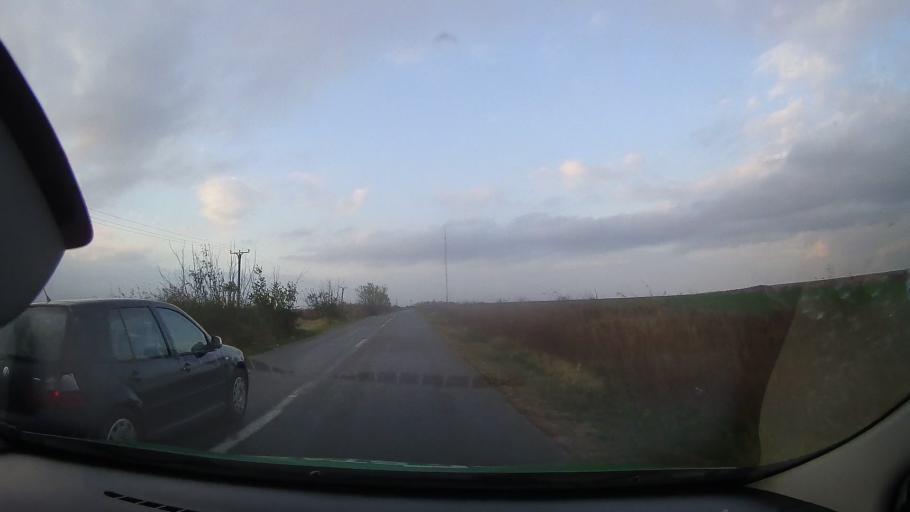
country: RO
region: Constanta
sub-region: Comuna Dobromir
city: Dobromir
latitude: 44.0410
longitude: 27.7566
